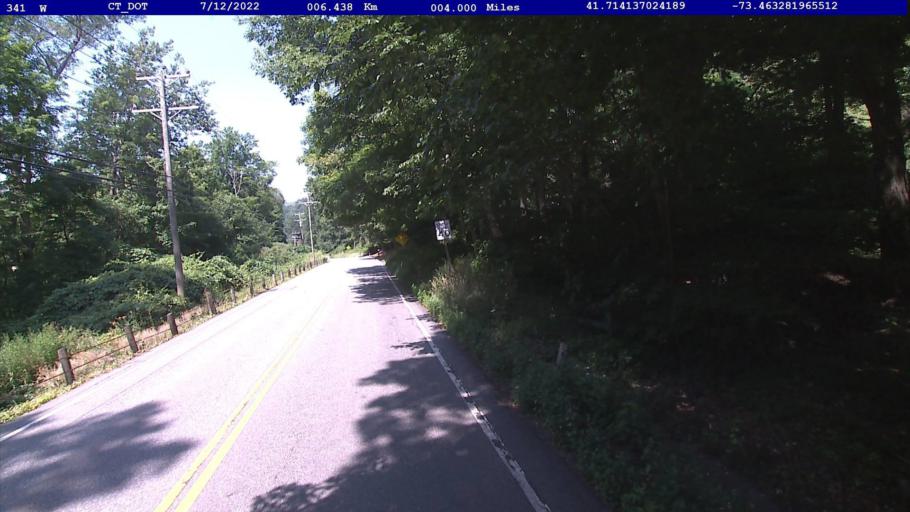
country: US
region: Connecticut
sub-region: Litchfield County
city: Kent
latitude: 41.7141
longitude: -73.4633
